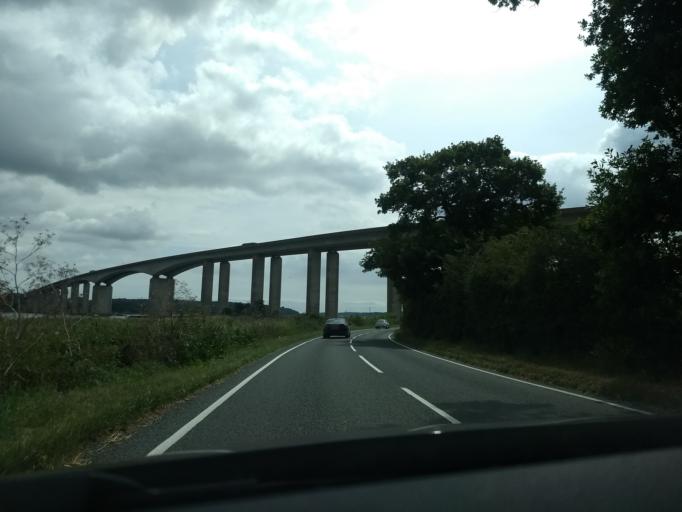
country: GB
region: England
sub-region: Suffolk
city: Ipswich
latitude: 52.0284
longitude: 1.1561
